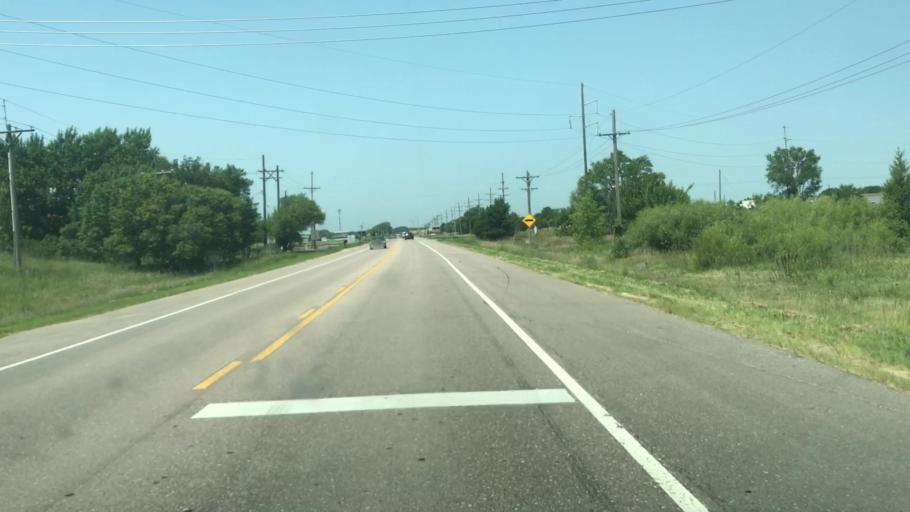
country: US
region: Nebraska
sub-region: Hall County
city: Grand Island
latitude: 40.8879
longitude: -98.3666
